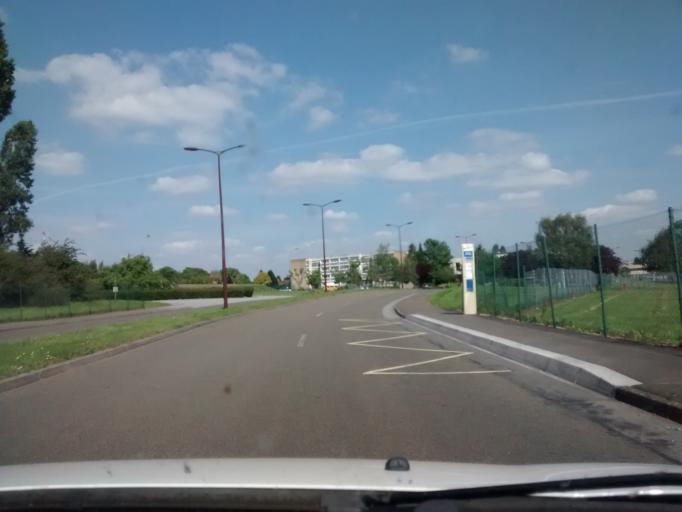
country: FR
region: Ile-de-France
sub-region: Departement des Yvelines
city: Buc
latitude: 48.7863
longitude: 2.1066
